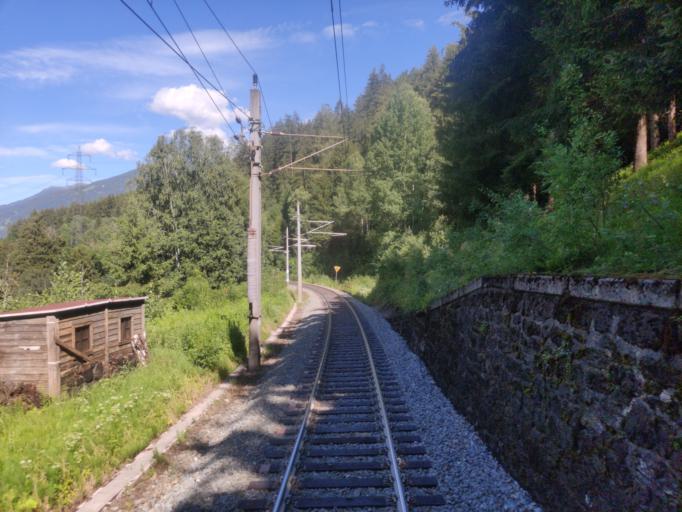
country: AT
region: Tyrol
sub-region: Politischer Bezirk Landeck
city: Grins
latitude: 47.1344
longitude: 10.5268
